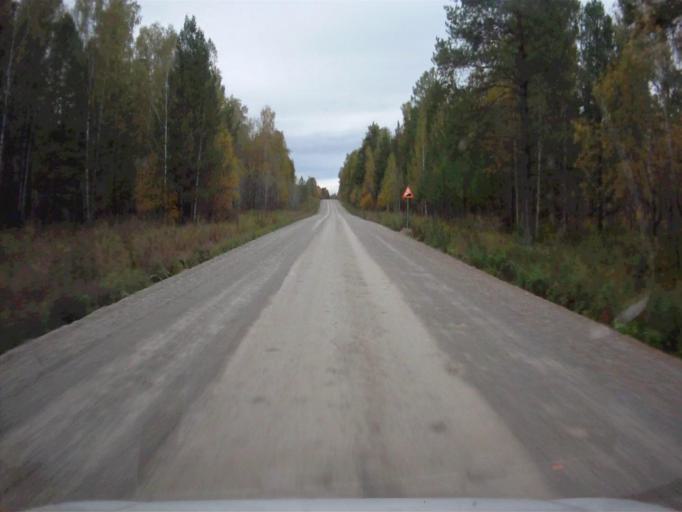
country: RU
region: Chelyabinsk
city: Nyazepetrovsk
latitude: 56.0771
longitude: 59.4255
